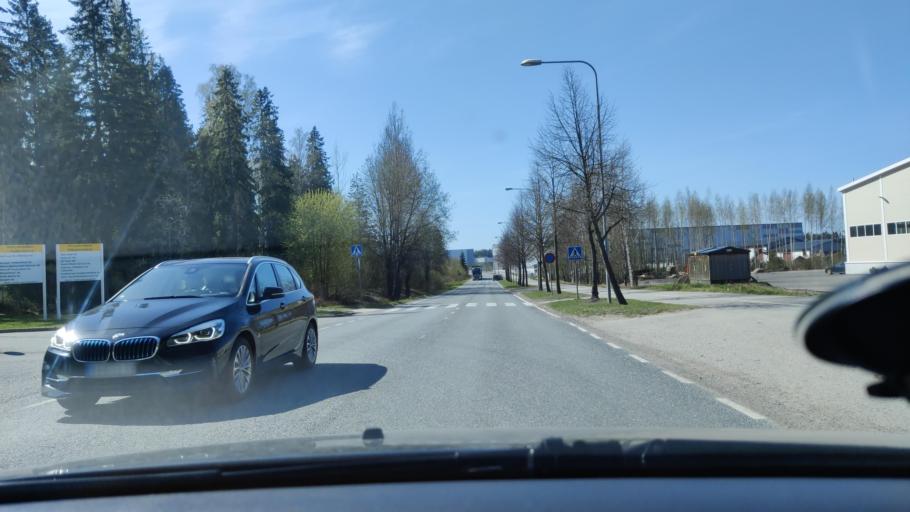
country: FI
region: Uusimaa
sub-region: Helsinki
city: Kerava
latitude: 60.3798
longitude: 25.1066
